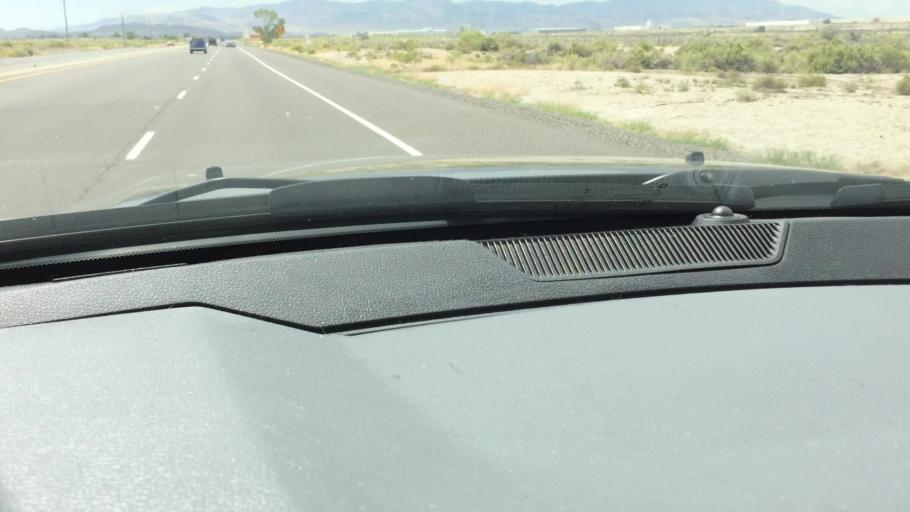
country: US
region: Nevada
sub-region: Lyon County
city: Fernley
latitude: 39.5957
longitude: -119.1769
